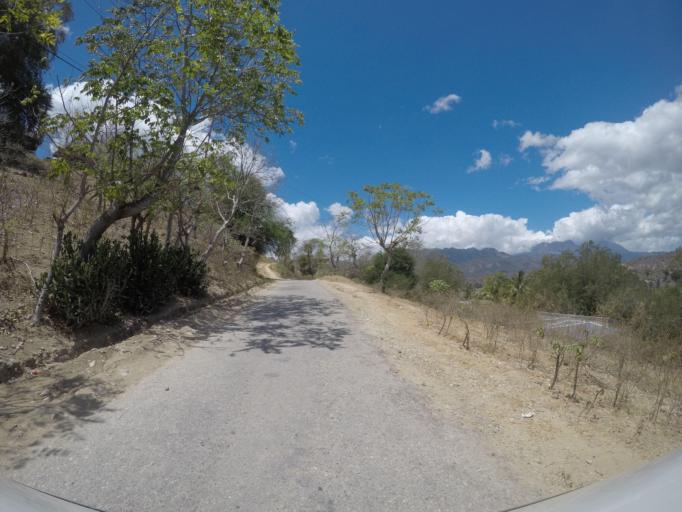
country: TL
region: Baucau
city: Baucau
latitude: -8.4775
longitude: 126.6019
